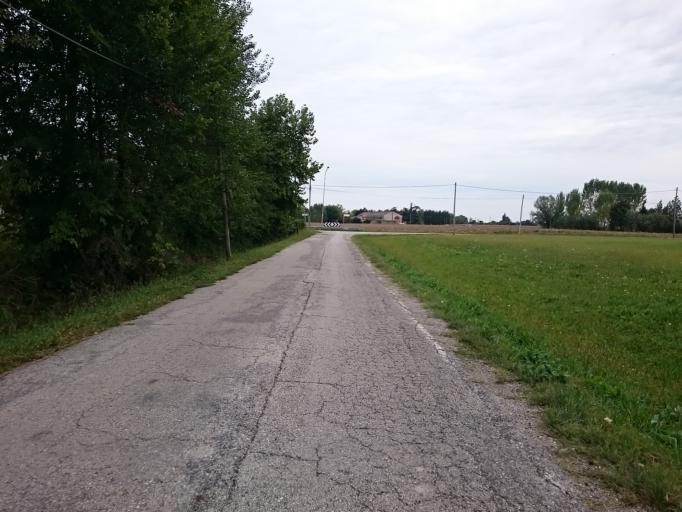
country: IT
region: Veneto
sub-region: Provincia di Vicenza
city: Quinto Vicentino
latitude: 45.5595
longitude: 11.6576
